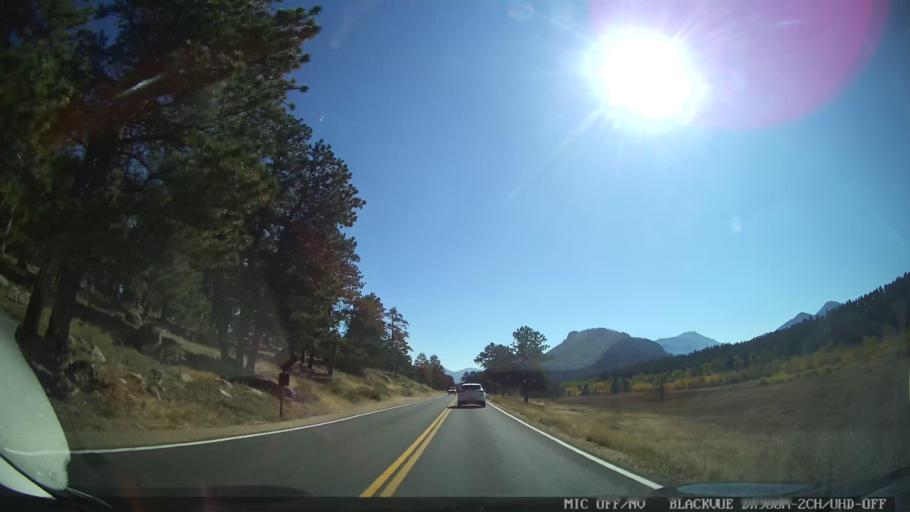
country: US
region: Colorado
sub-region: Larimer County
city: Estes Park
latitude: 40.3683
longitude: -105.5917
